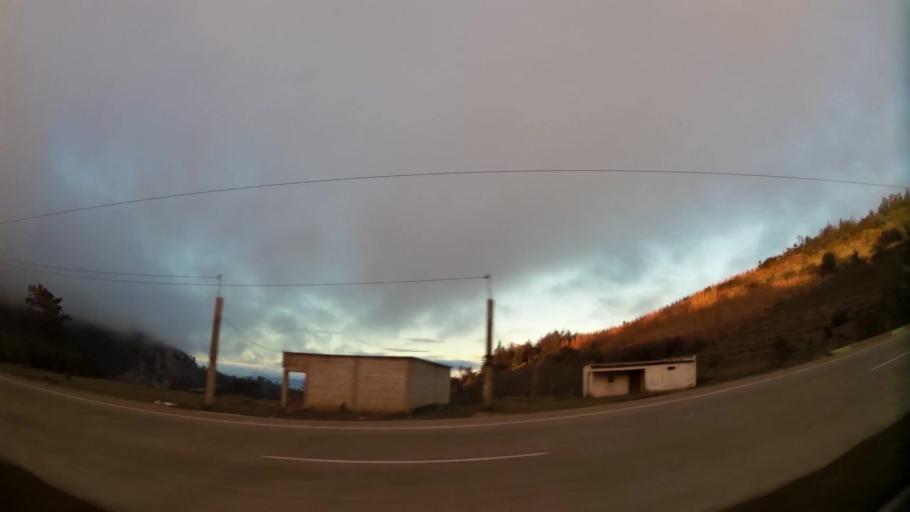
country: GT
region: Solola
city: Concepcion
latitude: 14.8374
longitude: -91.1281
